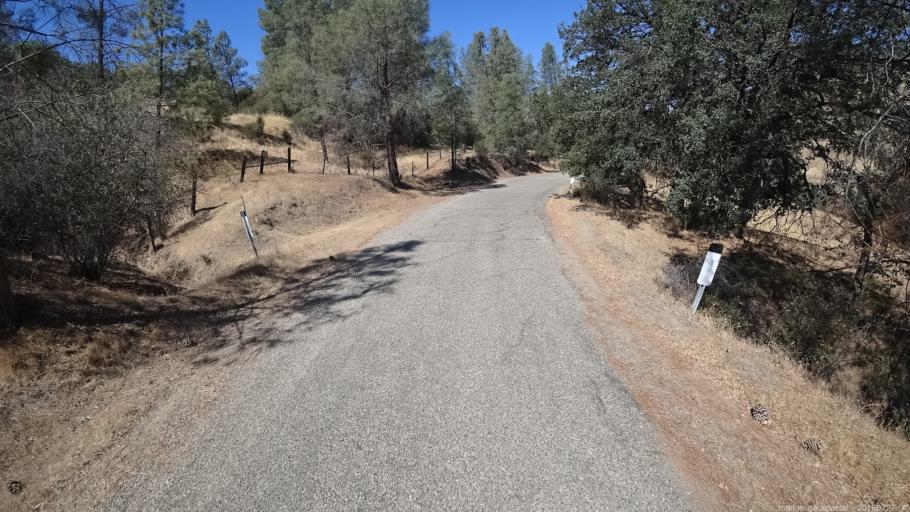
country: US
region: California
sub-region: Monterey County
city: King City
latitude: 36.2906
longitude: -120.8658
